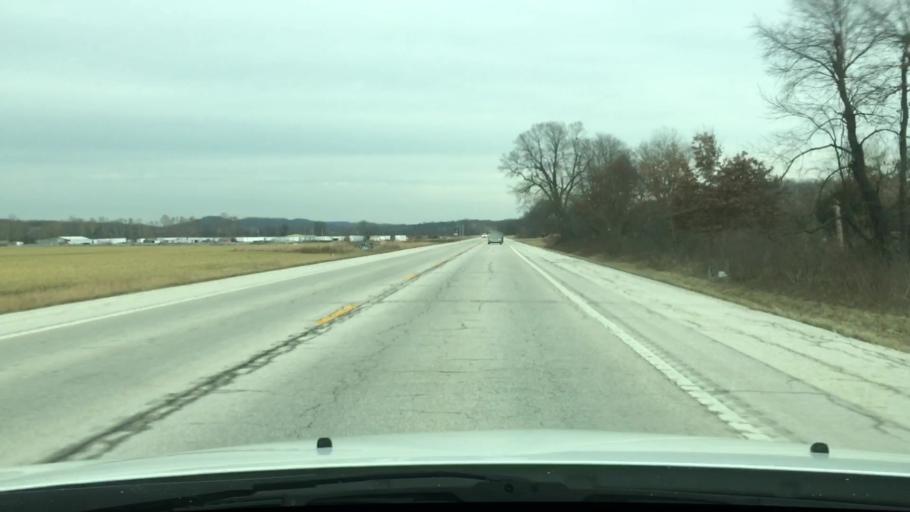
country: US
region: Missouri
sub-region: Pike County
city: Bowling Green
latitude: 39.3810
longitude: -91.1371
